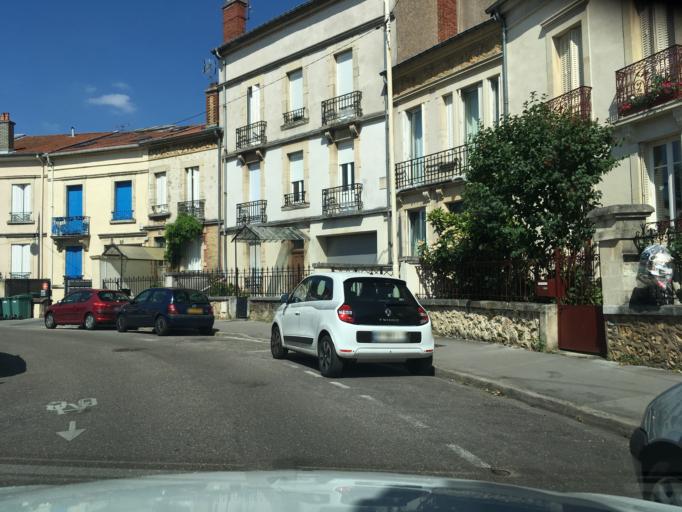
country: FR
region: Lorraine
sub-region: Departement de Meurthe-et-Moselle
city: Villers-les-Nancy
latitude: 48.6757
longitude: 6.1655
